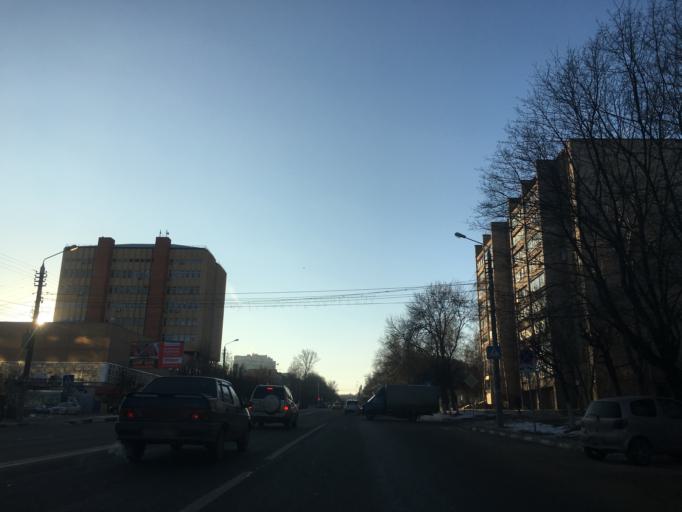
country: RU
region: Tula
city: Tula
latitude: 54.1933
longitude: 37.5912
